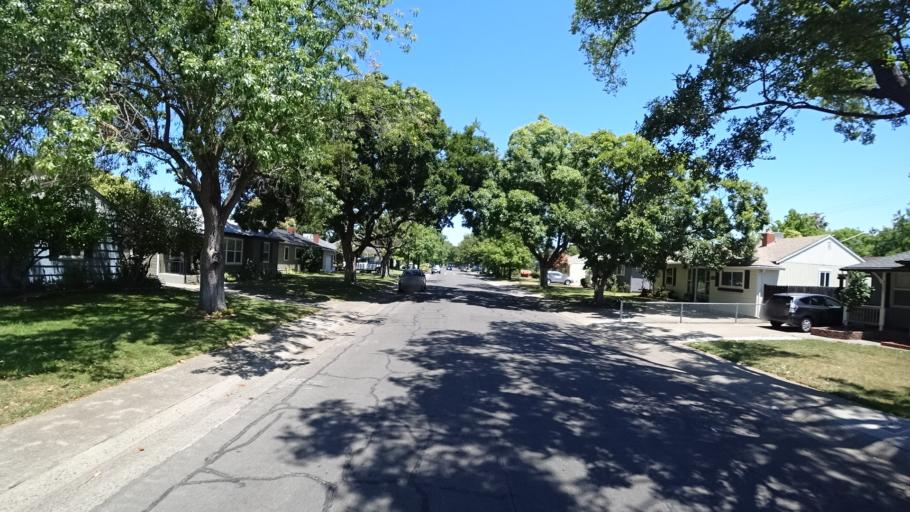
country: US
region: California
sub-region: Sacramento County
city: Florin
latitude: 38.5332
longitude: -121.4328
